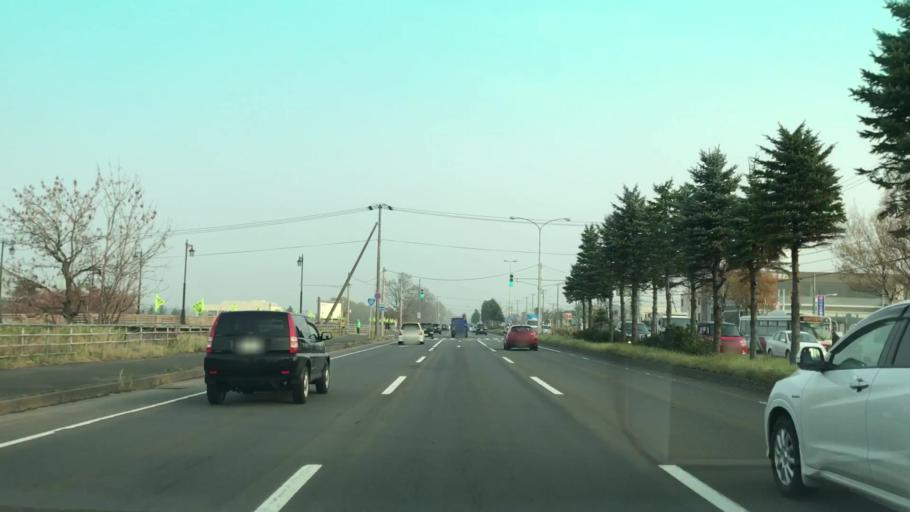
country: JP
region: Hokkaido
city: Sapporo
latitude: 43.1495
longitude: 141.3507
